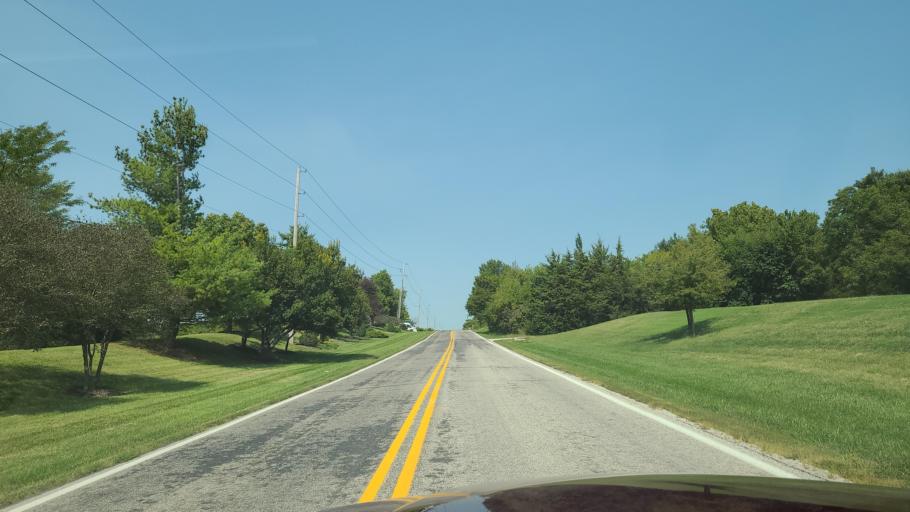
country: US
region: Kansas
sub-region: Douglas County
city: Lawrence
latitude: 38.9791
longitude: -95.2976
